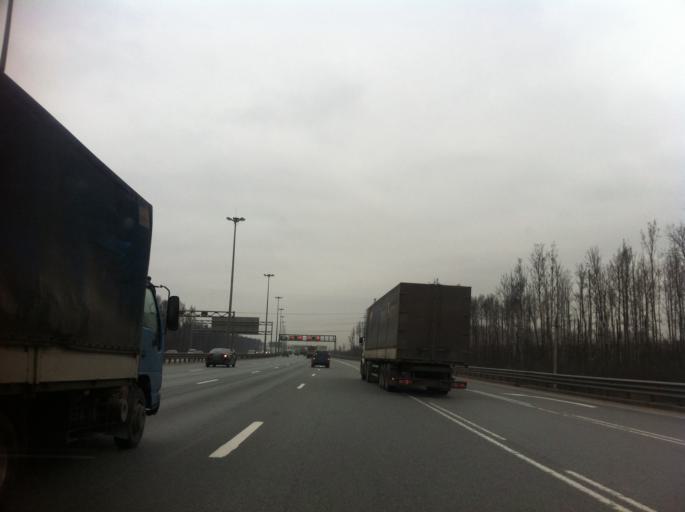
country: RU
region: Leningrad
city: Rybatskoye
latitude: 59.8872
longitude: 30.5245
